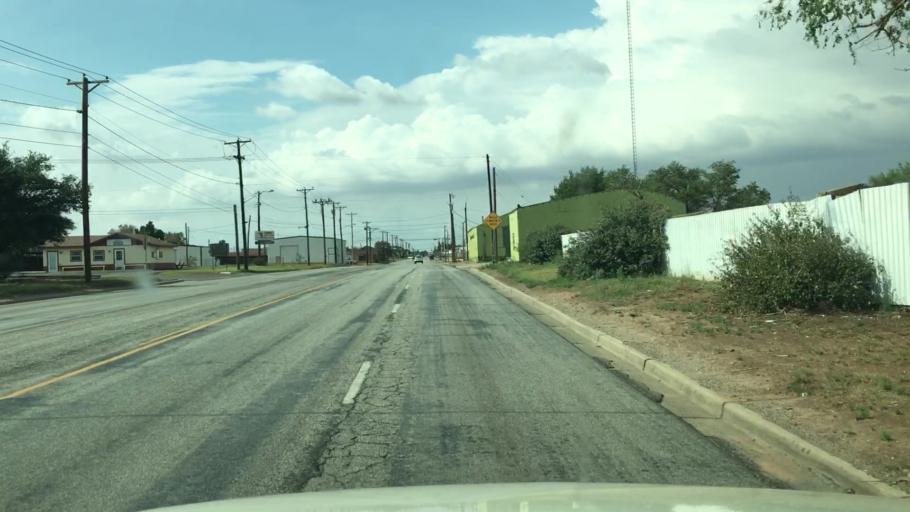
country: US
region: Texas
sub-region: Dawson County
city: Lamesa
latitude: 32.7312
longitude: -101.9485
